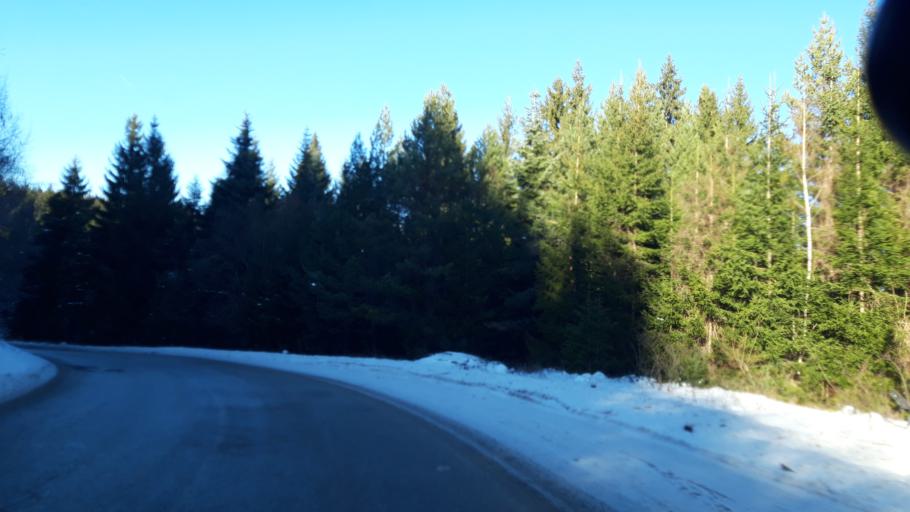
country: BA
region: Republika Srpska
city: Koran
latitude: 43.7975
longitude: 18.5549
